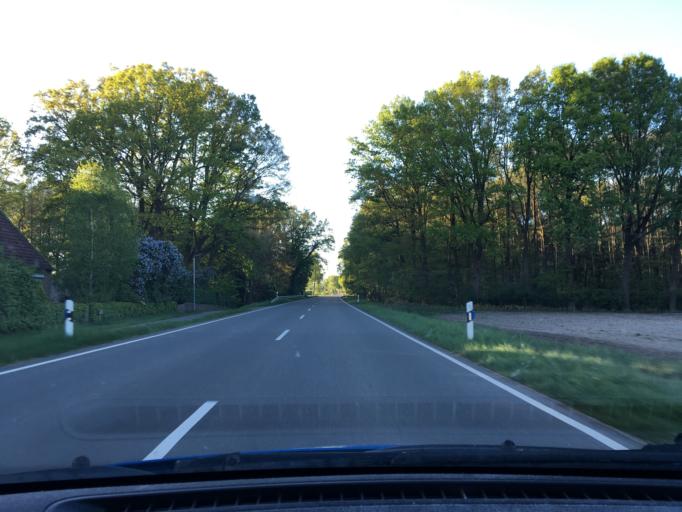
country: DE
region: Lower Saxony
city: Oldendorf
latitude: 53.1690
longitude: 10.2113
